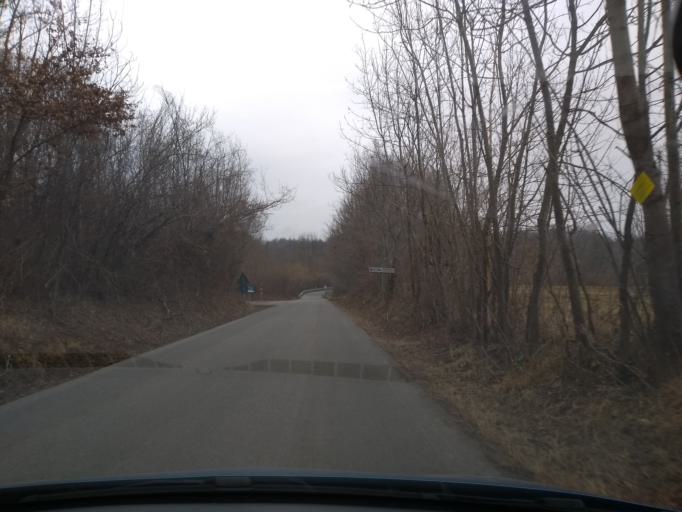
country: IT
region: Piedmont
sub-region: Provincia di Biella
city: Torrazzo
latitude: 45.4868
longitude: 7.9707
